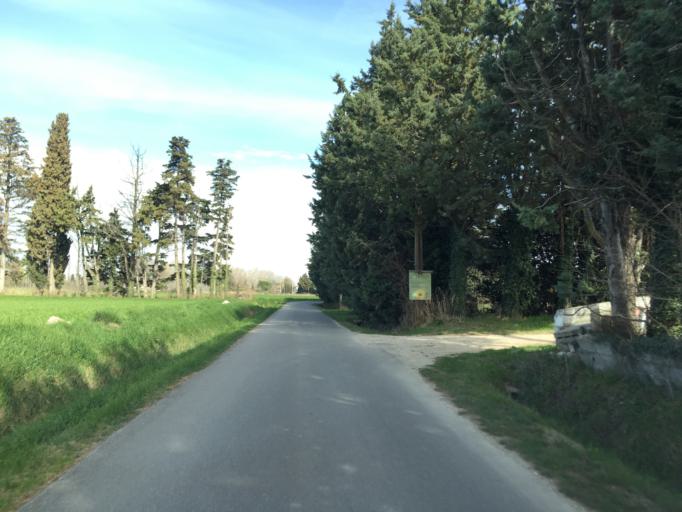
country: FR
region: Provence-Alpes-Cote d'Azur
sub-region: Departement du Vaucluse
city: Caderousse
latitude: 44.1125
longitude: 4.7425
